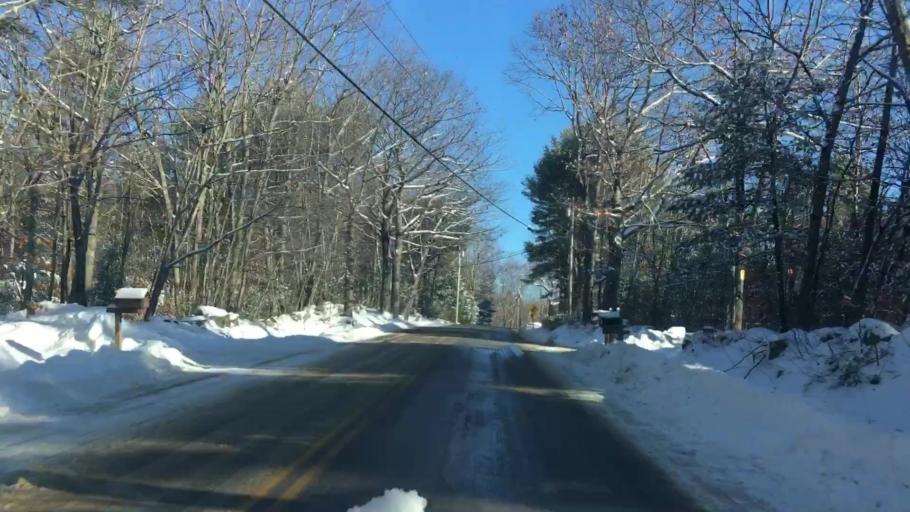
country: US
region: Maine
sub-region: Cumberland County
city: New Gloucester
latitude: 43.9574
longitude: -70.3221
